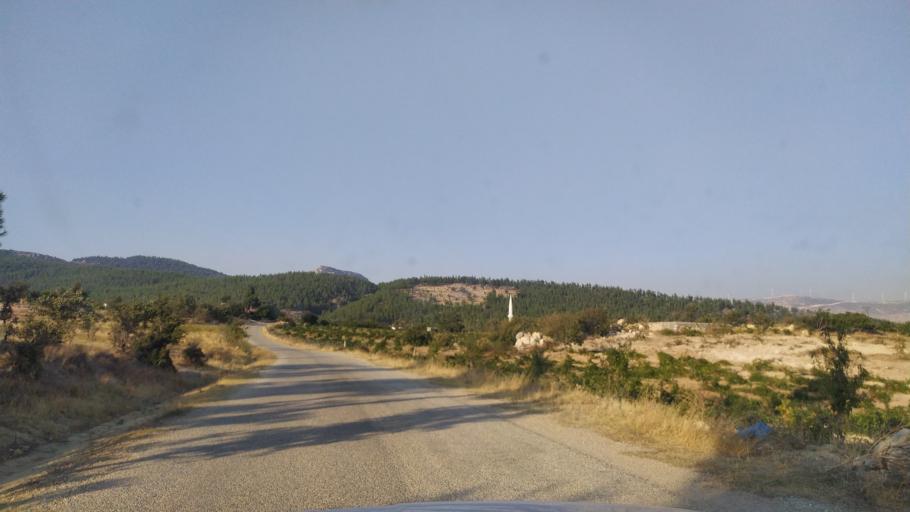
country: TR
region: Mersin
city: Mut
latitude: 36.6900
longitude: 33.1982
